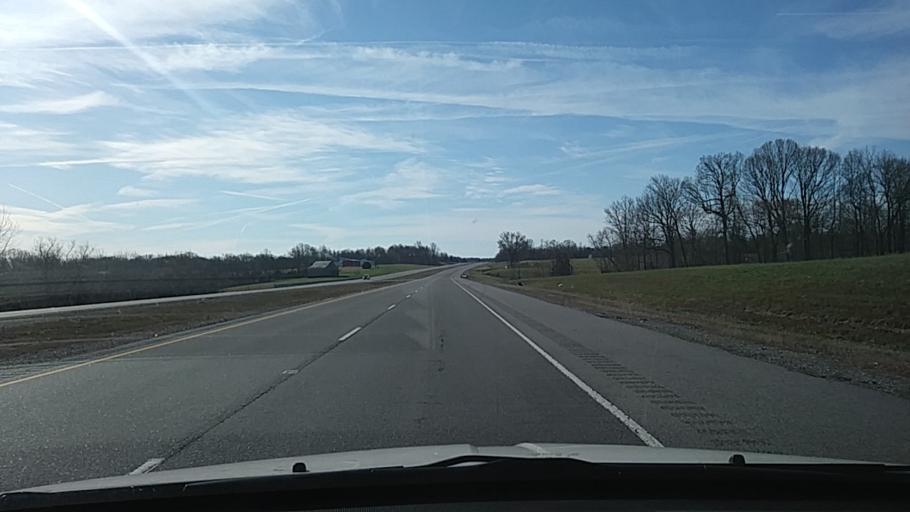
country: US
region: Tennessee
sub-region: Sumner County
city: Portland
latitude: 36.5064
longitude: -86.5032
